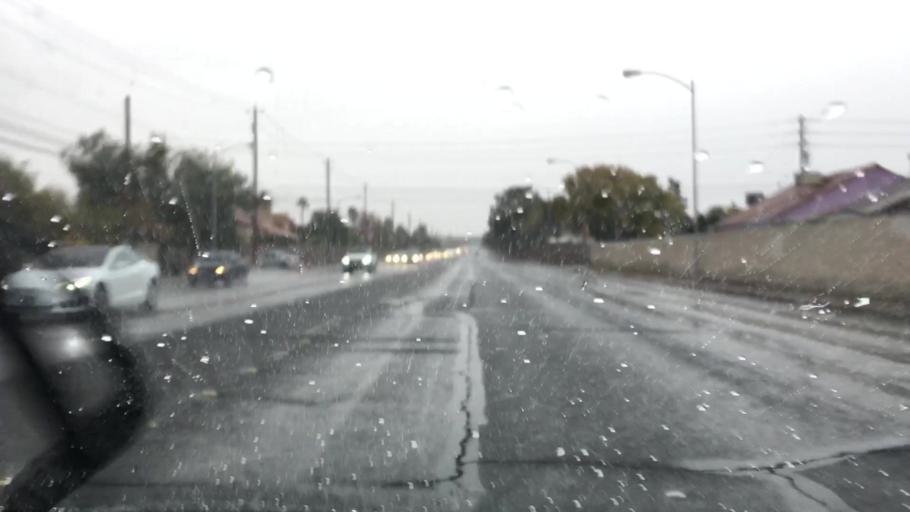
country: US
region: Nevada
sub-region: Clark County
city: Paradise
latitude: 36.0576
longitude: -115.1310
